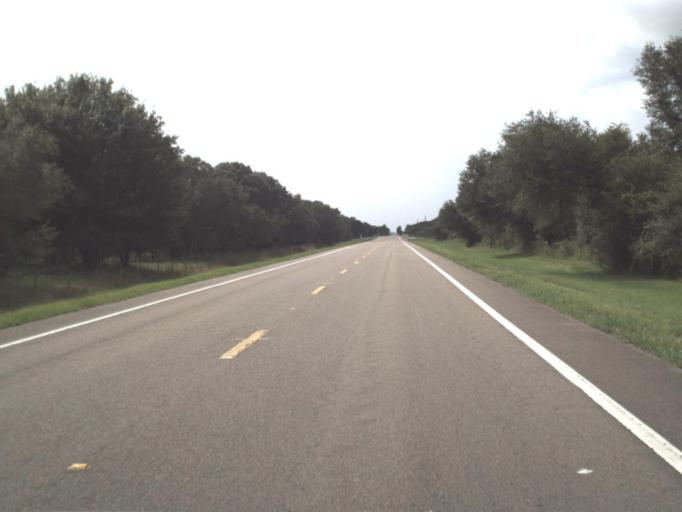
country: US
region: Florida
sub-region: Sarasota County
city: North Port
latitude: 27.1933
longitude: -82.1391
